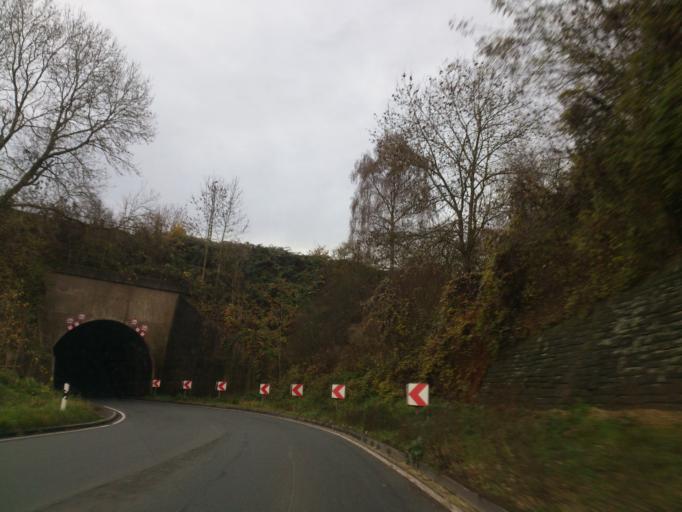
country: DE
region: North Rhine-Westphalia
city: Beverungen
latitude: 51.7110
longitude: 9.3145
